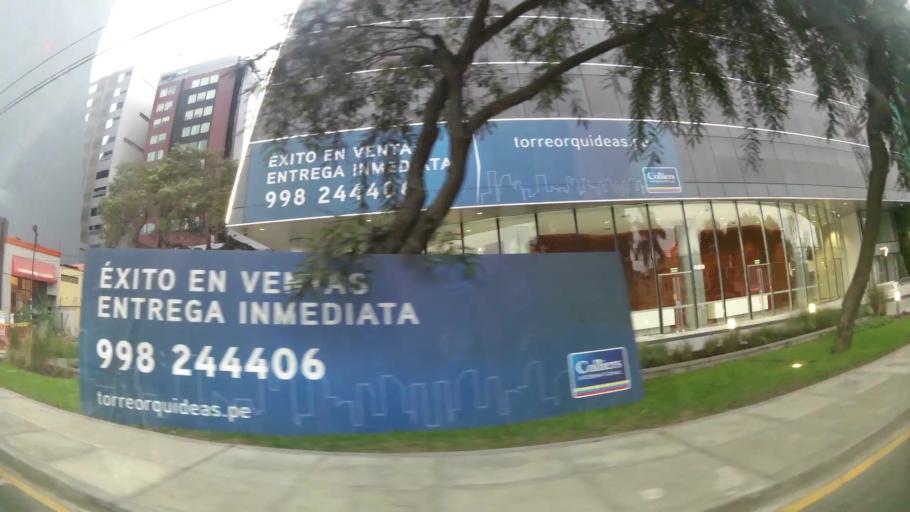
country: PE
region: Lima
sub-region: Lima
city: San Isidro
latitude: -12.0918
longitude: -77.0283
